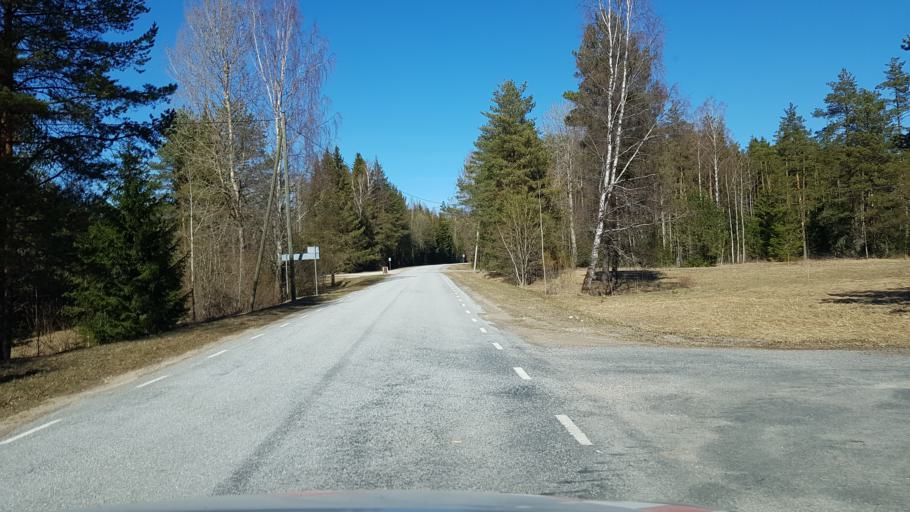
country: EE
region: Laeaene-Virumaa
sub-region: Viru-Nigula vald
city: Kunda
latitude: 59.3266
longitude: 26.6231
